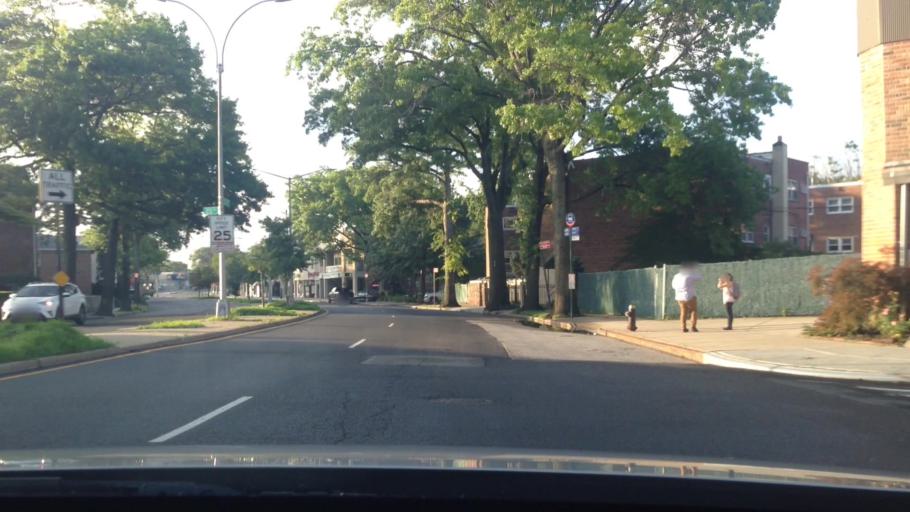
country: US
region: New York
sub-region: Nassau County
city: East Atlantic Beach
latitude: 40.7745
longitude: -73.7980
